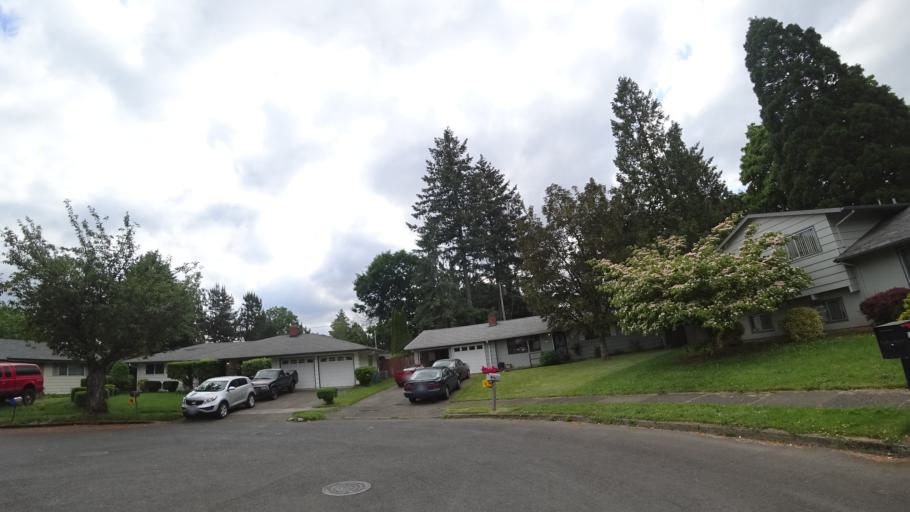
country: US
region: Oregon
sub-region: Multnomah County
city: Gresham
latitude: 45.5130
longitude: -122.4874
